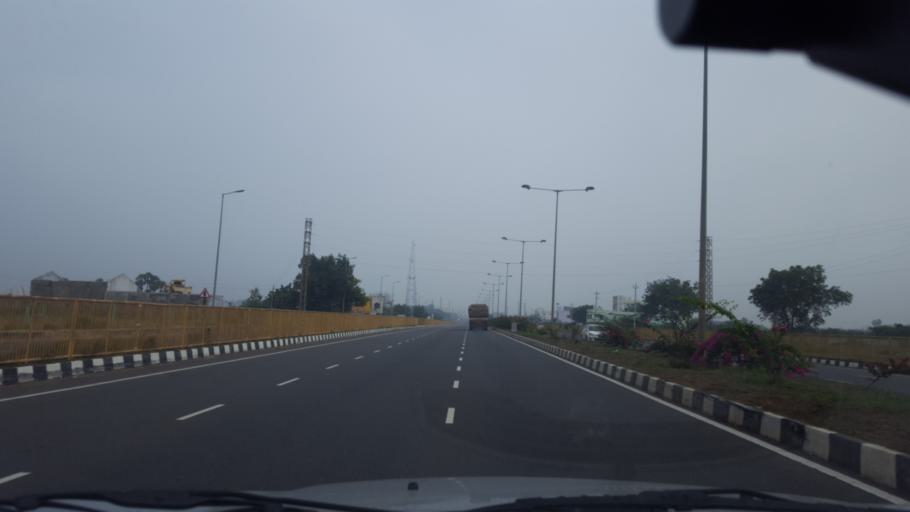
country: IN
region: Andhra Pradesh
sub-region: Prakasam
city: pedda nakkalapalem
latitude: 15.9703
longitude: 80.0956
